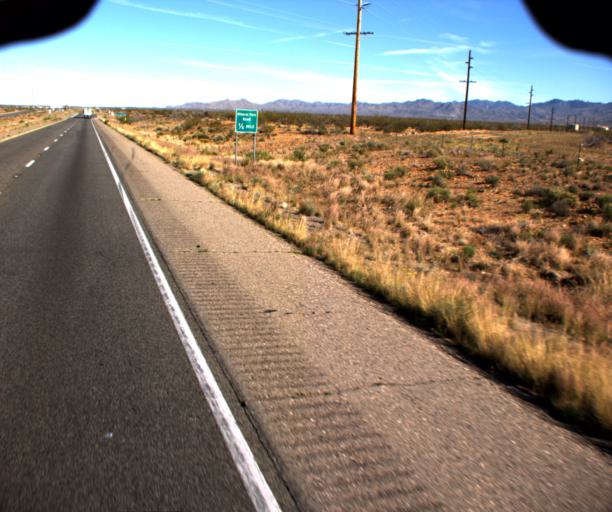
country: US
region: Arizona
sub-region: Mohave County
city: Golden Valley
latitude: 35.3195
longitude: -114.2032
